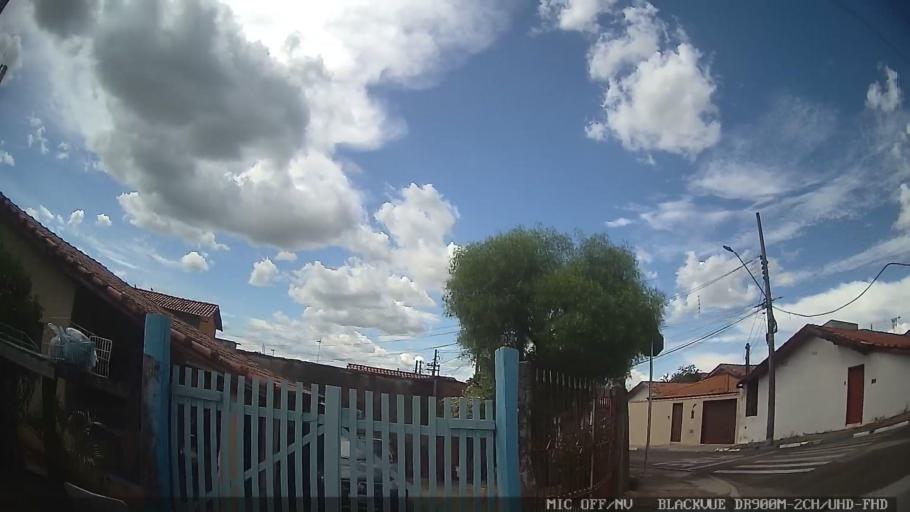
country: BR
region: Sao Paulo
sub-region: Conchas
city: Conchas
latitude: -23.0206
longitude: -48.0165
